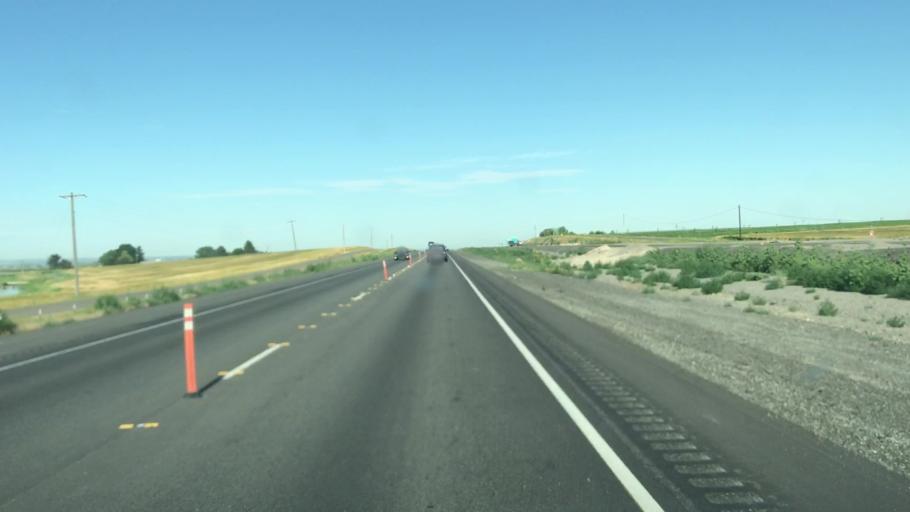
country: US
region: Idaho
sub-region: Twin Falls County
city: Hansen
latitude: 42.5761
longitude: -114.2424
